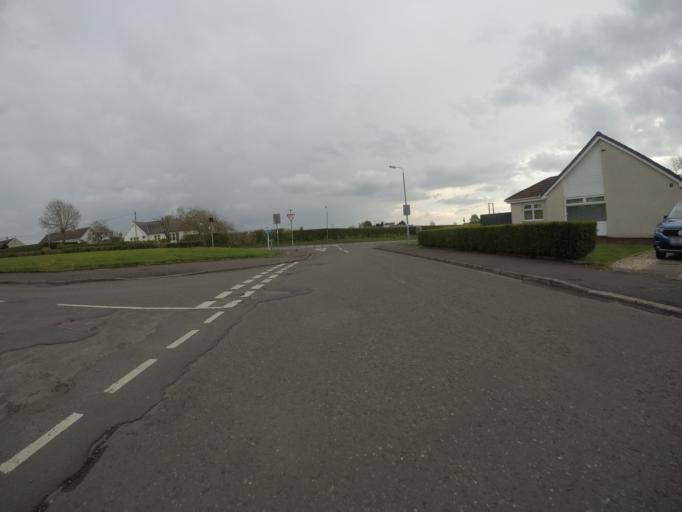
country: GB
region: Scotland
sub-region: East Ayrshire
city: Kilmaurs
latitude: 55.6398
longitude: -4.5378
